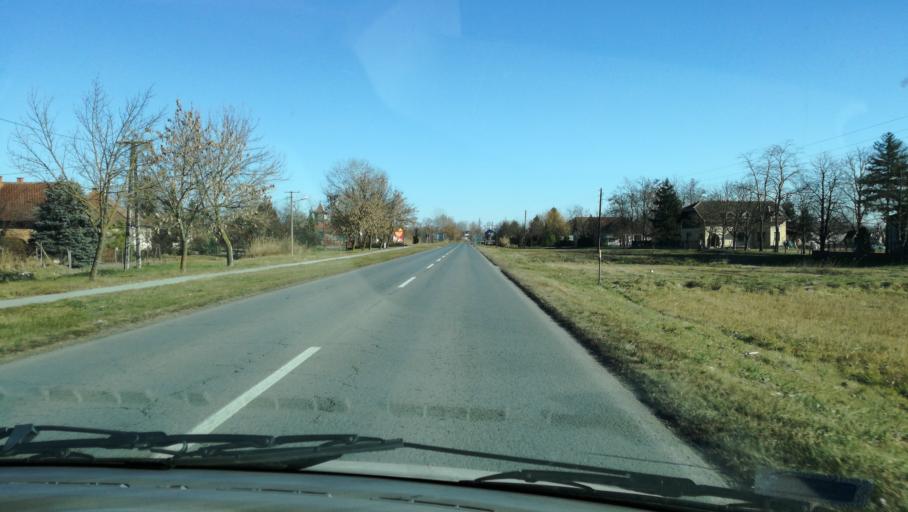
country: HU
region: Csongrad
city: Asotthalom
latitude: 46.1083
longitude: 19.8044
